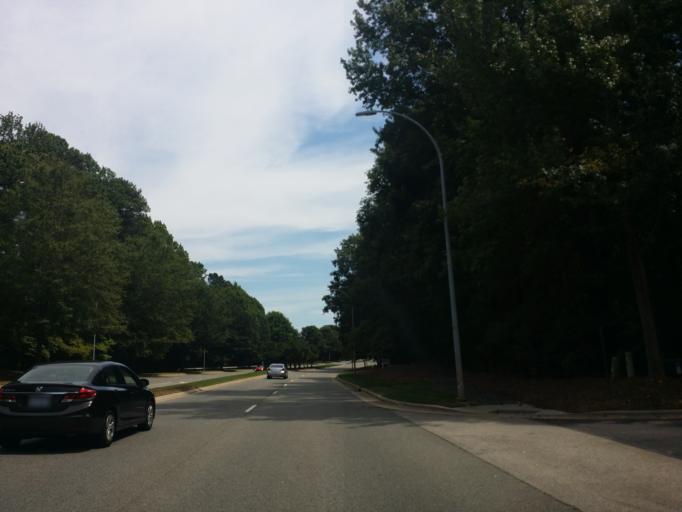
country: US
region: North Carolina
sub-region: Wake County
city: Cary
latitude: 35.8308
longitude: -78.7766
